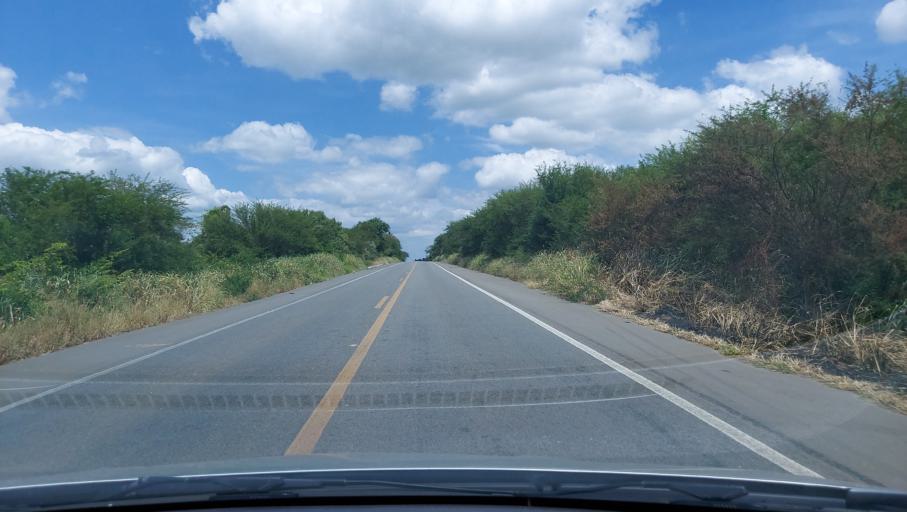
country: BR
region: Bahia
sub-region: Andarai
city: Vera Cruz
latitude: -12.4687
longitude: -40.9477
